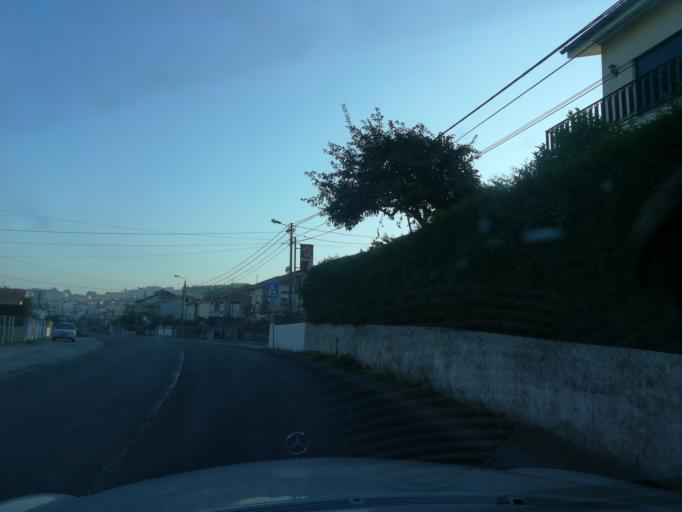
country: PT
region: Braga
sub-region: Braga
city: Braga
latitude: 41.5234
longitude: -8.4309
